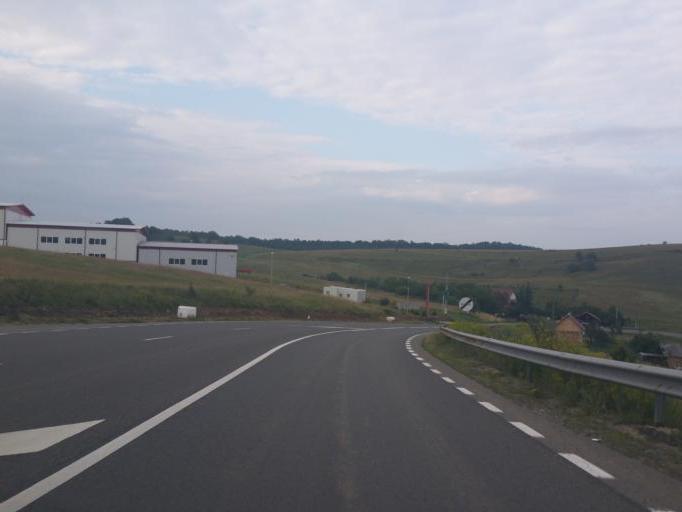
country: RO
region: Cluj
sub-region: Comuna Sanpaul
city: Sanpaul
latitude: 46.9408
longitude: 23.3864
